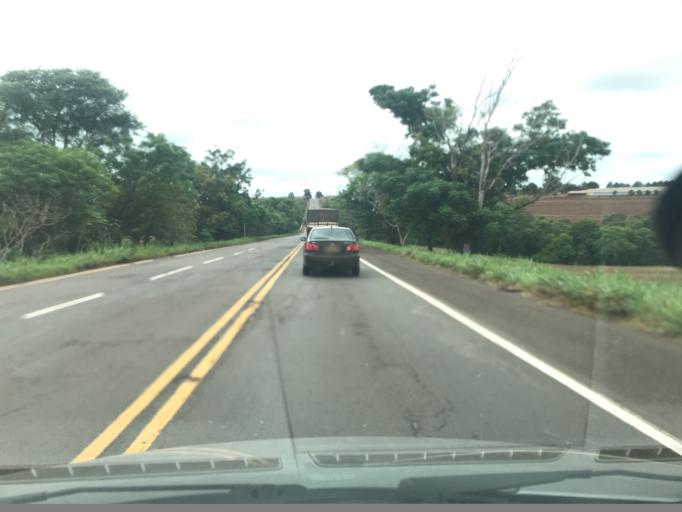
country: BR
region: Parana
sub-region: Terra Boa
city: Terra Boa
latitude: -23.6168
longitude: -52.4329
